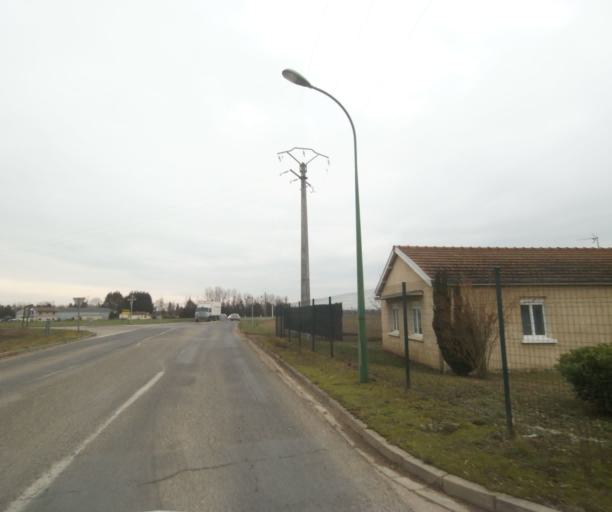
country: FR
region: Champagne-Ardenne
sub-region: Departement de la Haute-Marne
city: Villiers-en-Lieu
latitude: 48.6571
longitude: 4.9092
